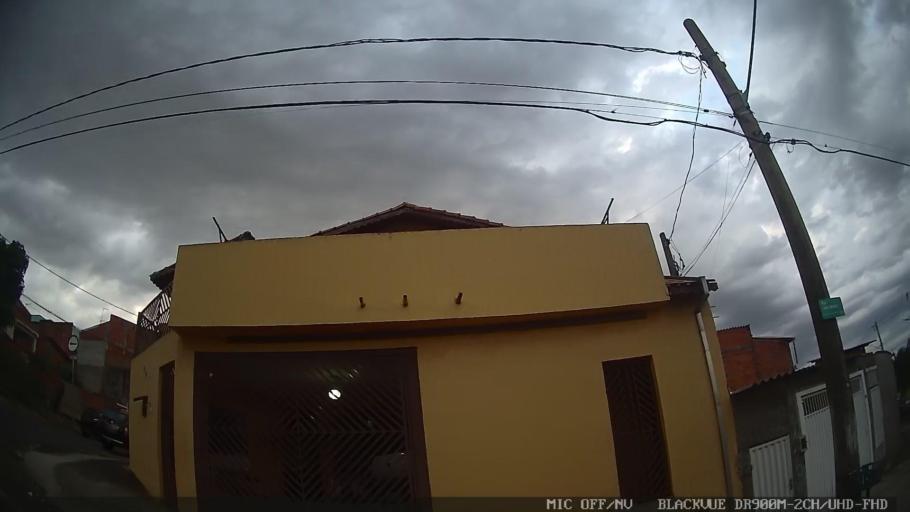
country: BR
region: Sao Paulo
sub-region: Indaiatuba
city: Indaiatuba
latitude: -23.1311
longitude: -47.2449
